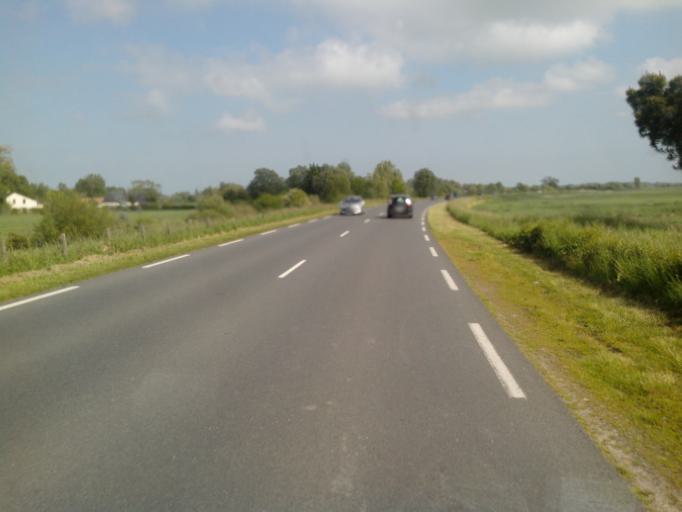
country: FR
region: Picardie
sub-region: Departement de la Somme
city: Saint-Valery-sur-Somme
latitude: 50.2099
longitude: 1.6763
